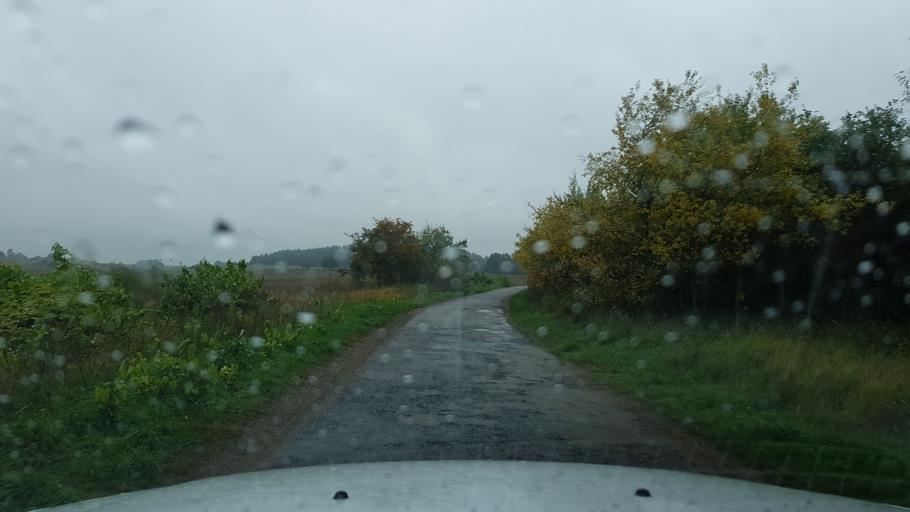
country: PL
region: West Pomeranian Voivodeship
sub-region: Powiat mysliborski
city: Barlinek
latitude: 53.0417
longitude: 15.2406
